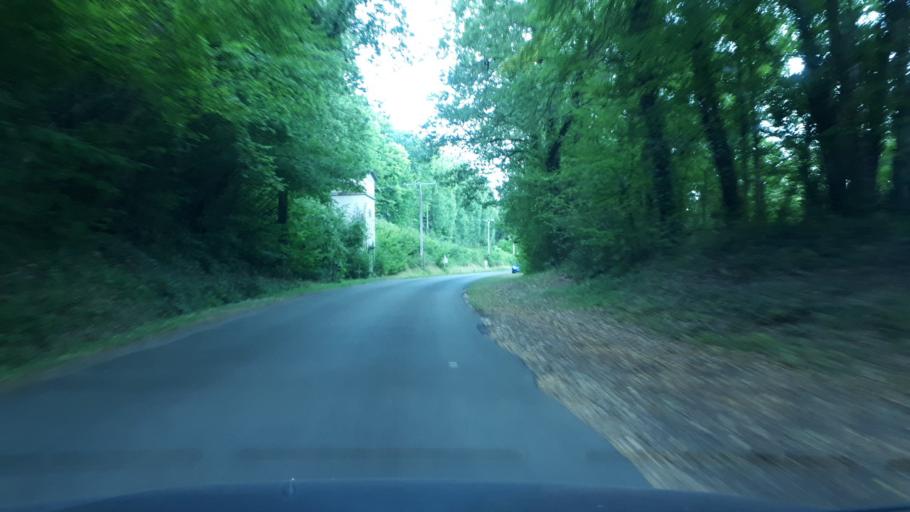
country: FR
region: Centre
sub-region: Departement du Loir-et-Cher
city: Villiers-sur-Loir
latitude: 47.7718
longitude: 0.9608
